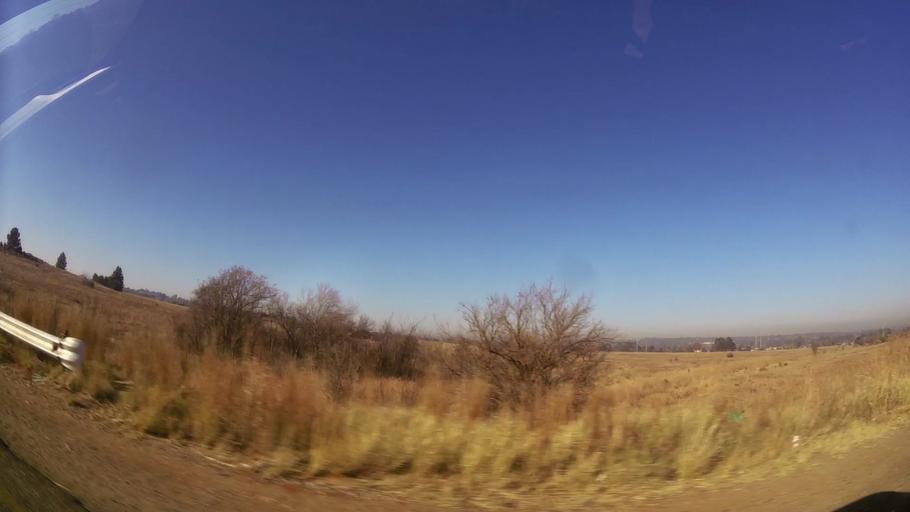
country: ZA
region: Gauteng
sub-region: City of Tshwane Metropolitan Municipality
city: Centurion
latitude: -25.8221
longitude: 28.1730
